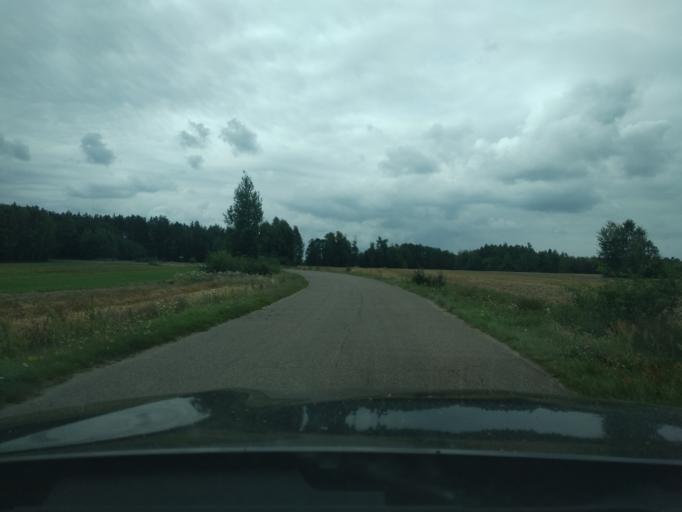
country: PL
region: Masovian Voivodeship
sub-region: Powiat pultuski
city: Obryte
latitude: 52.7454
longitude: 21.2147
